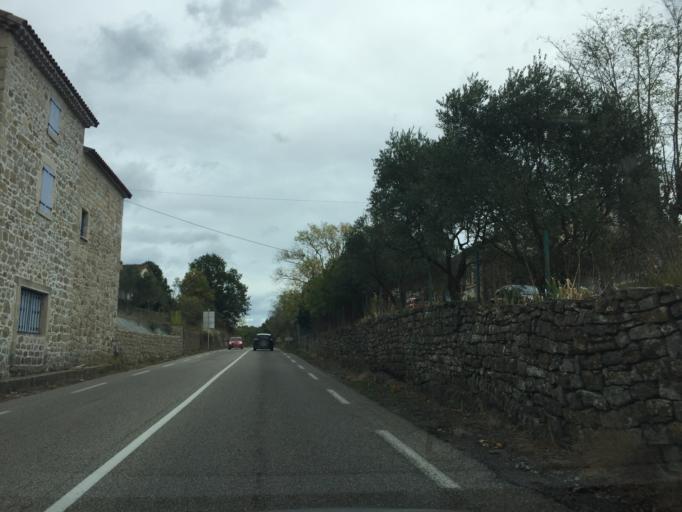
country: FR
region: Rhone-Alpes
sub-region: Departement de l'Ardeche
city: Lablachere
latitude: 44.4332
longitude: 4.1906
